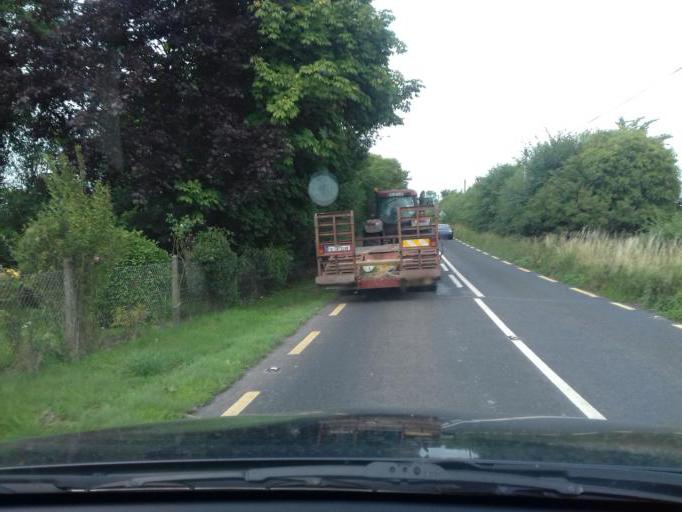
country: IE
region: Leinster
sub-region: County Carlow
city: Tullow
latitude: 52.8379
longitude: -6.7197
